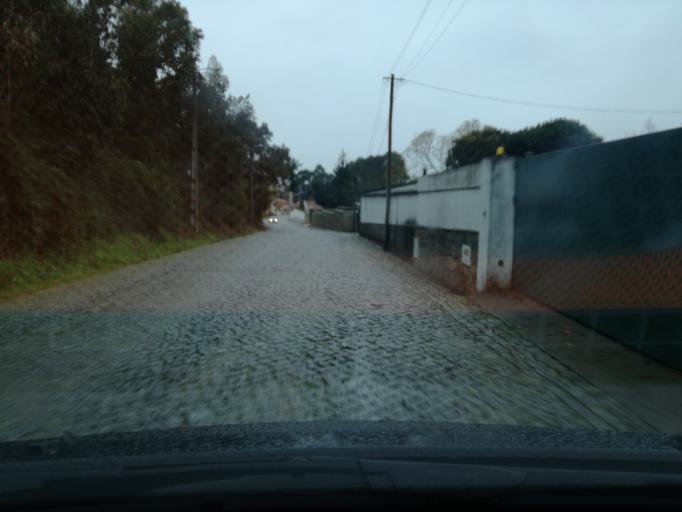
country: PT
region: Porto
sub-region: Maia
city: Gemunde
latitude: 41.2575
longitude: -8.6590
